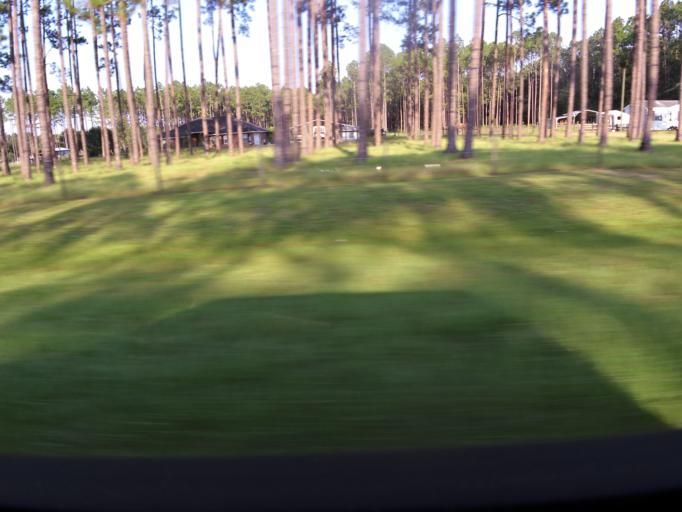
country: US
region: Florida
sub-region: Duval County
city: Baldwin
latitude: 30.3107
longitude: -82.0084
